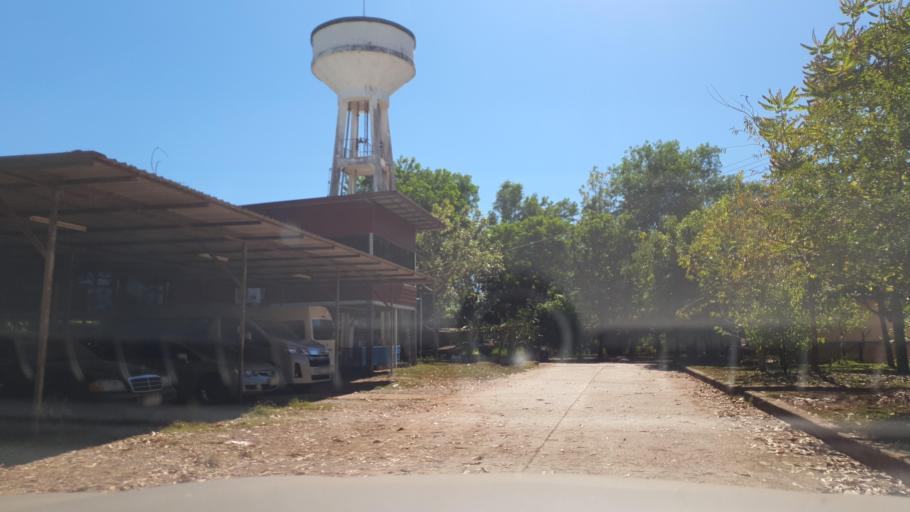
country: TH
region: Nakhon Phanom
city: Nakhon Phanom
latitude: 17.3740
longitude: 104.7371
